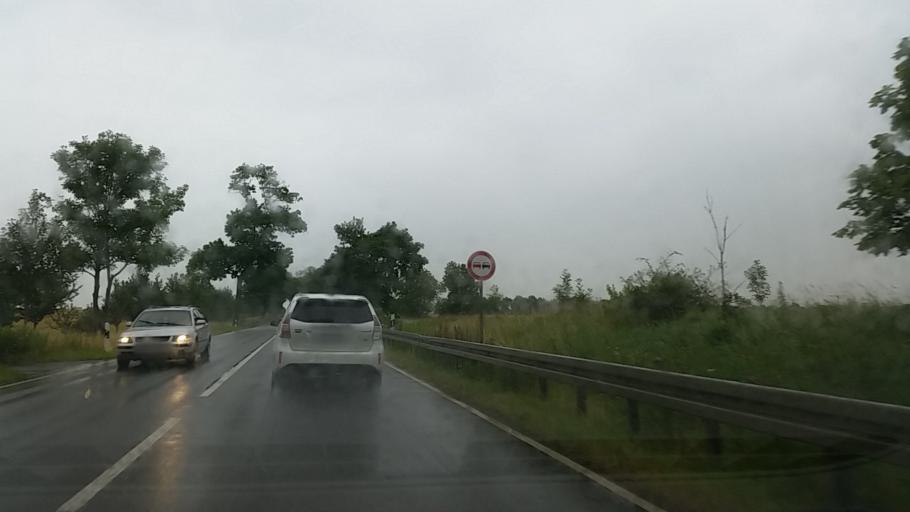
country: DE
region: Mecklenburg-Vorpommern
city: Kropelin
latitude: 54.0784
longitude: 11.8327
